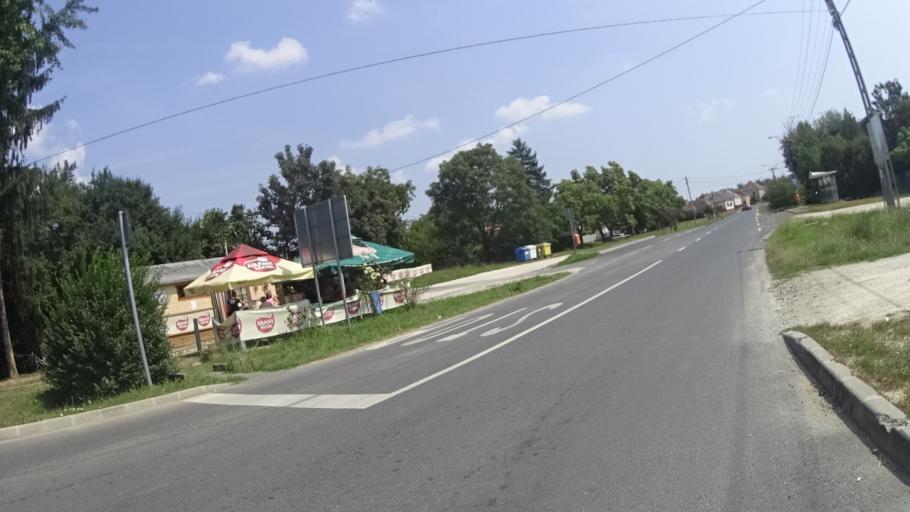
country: HU
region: Zala
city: Letenye
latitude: 46.4257
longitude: 16.7231
